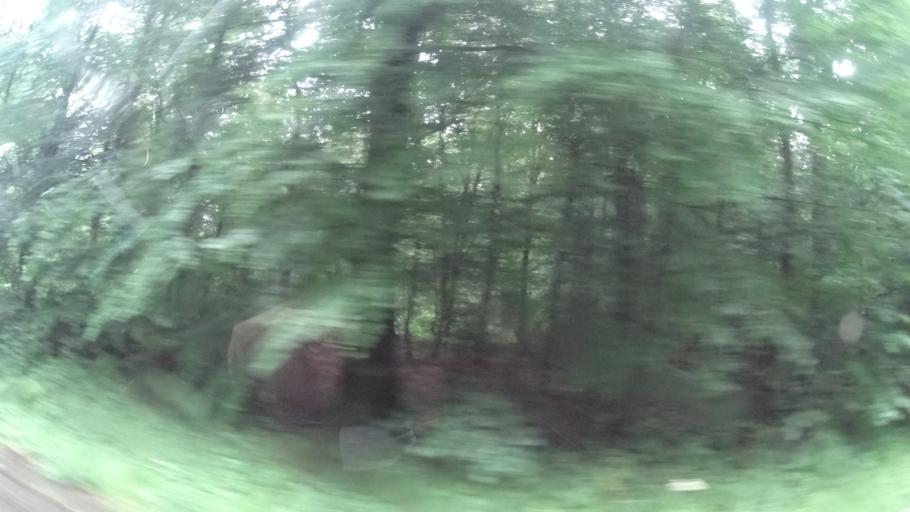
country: BE
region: Wallonia
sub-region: Province de Namur
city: Bievre
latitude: 49.9379
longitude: 5.0775
